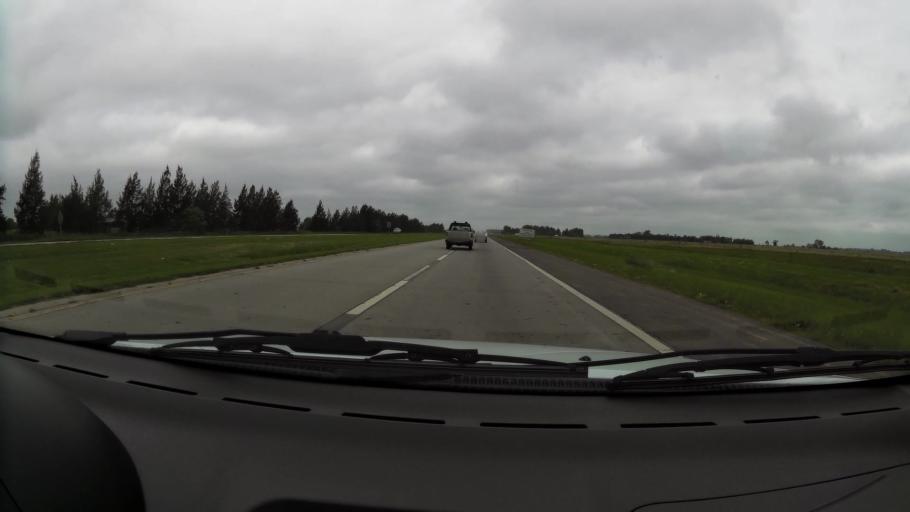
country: AR
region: Buenos Aires
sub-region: Partido de Brandsen
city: Brandsen
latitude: -35.0444
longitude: -58.1631
